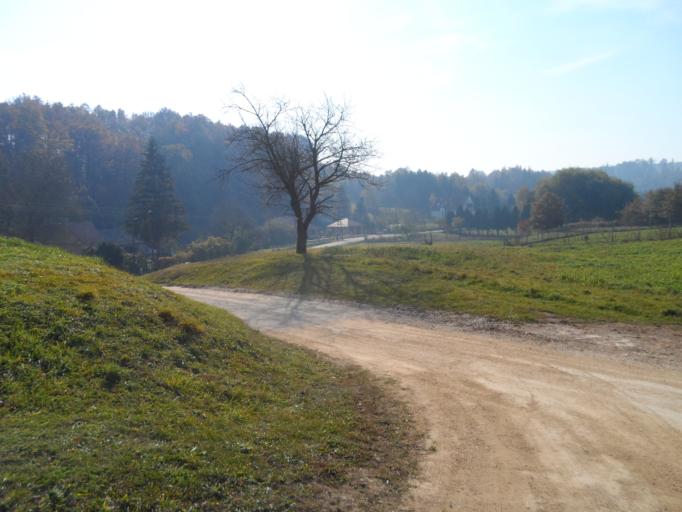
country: HU
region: Veszprem
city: Herend
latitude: 47.2183
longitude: 17.6513
